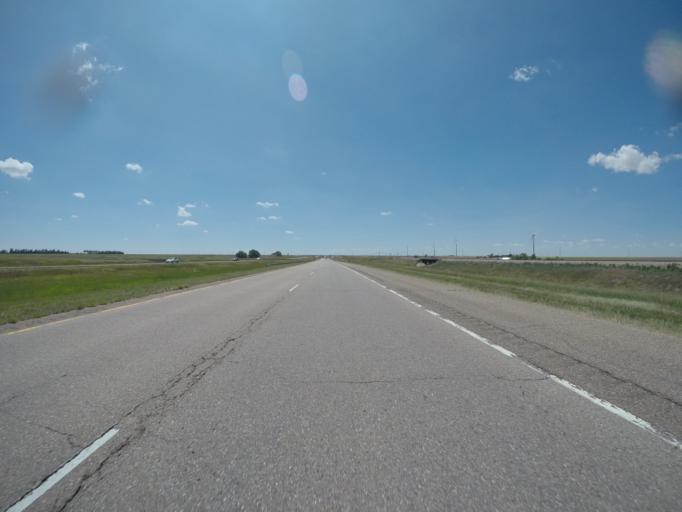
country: US
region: Colorado
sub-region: Lincoln County
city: Hugo
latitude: 39.2799
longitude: -103.3831
